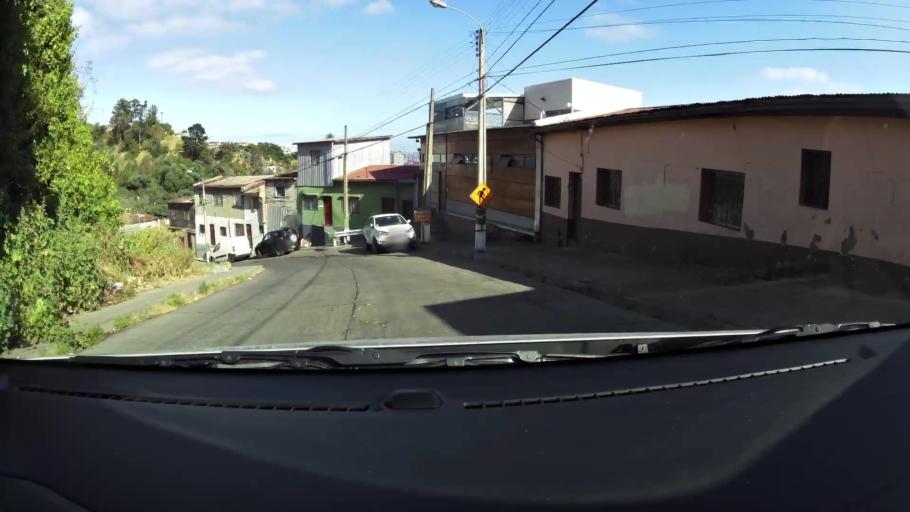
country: CL
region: Valparaiso
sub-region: Provincia de Valparaiso
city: Valparaiso
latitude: -33.0547
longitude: -71.6006
